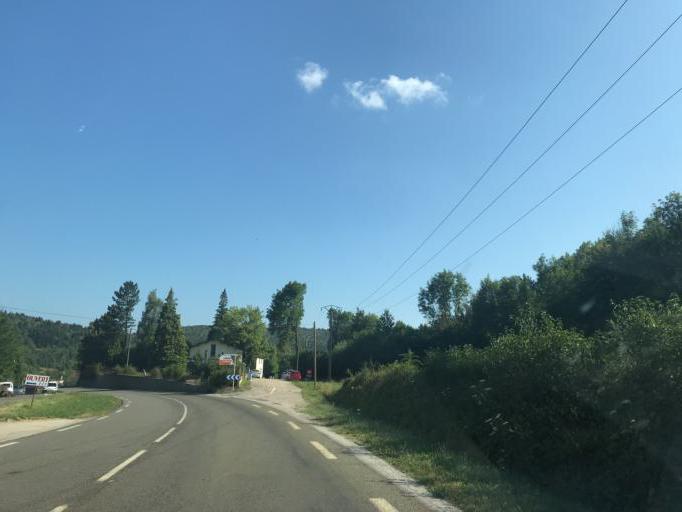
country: FR
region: Franche-Comte
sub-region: Departement du Jura
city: Moirans-en-Montagne
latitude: 46.4080
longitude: 5.7345
